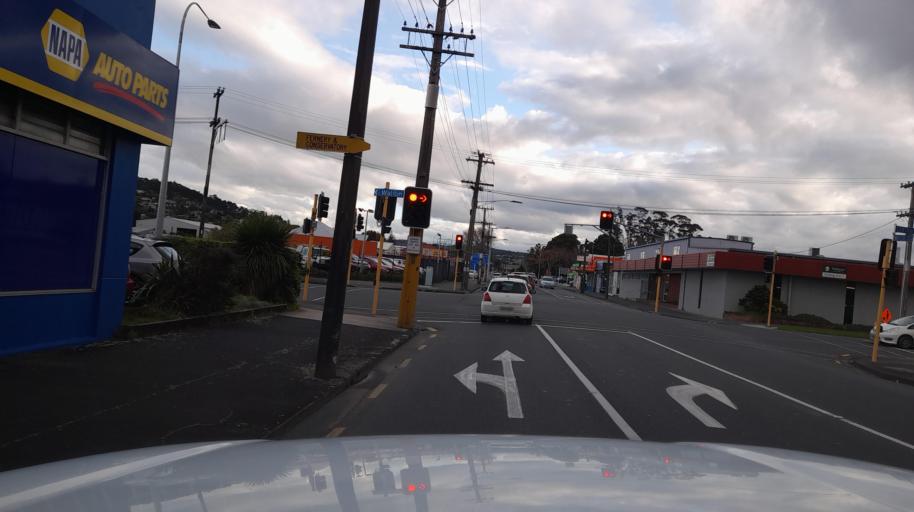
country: NZ
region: Northland
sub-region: Whangarei
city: Whangarei
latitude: -35.7273
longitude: 174.3168
